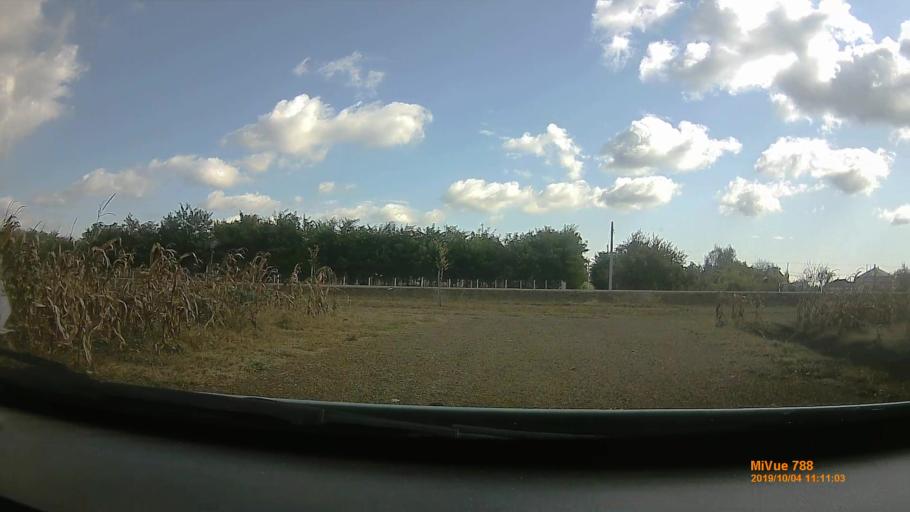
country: HU
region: Szabolcs-Szatmar-Bereg
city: Nyirtelek
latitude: 47.9966
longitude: 21.6739
